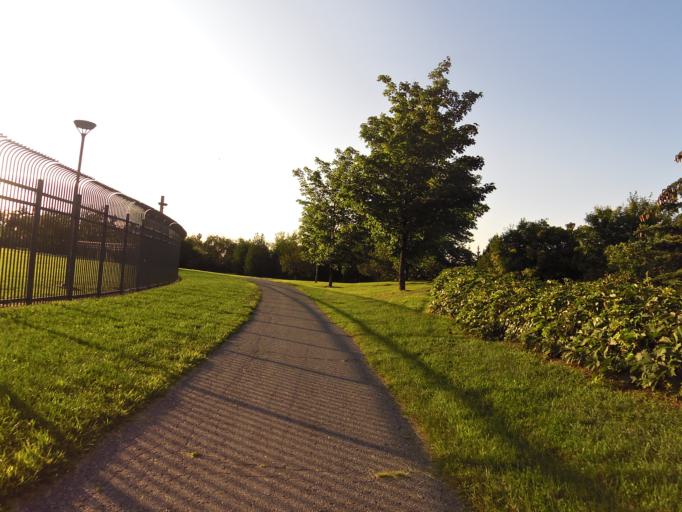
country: CA
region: Ontario
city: Ottawa
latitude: 45.3788
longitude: -75.6859
